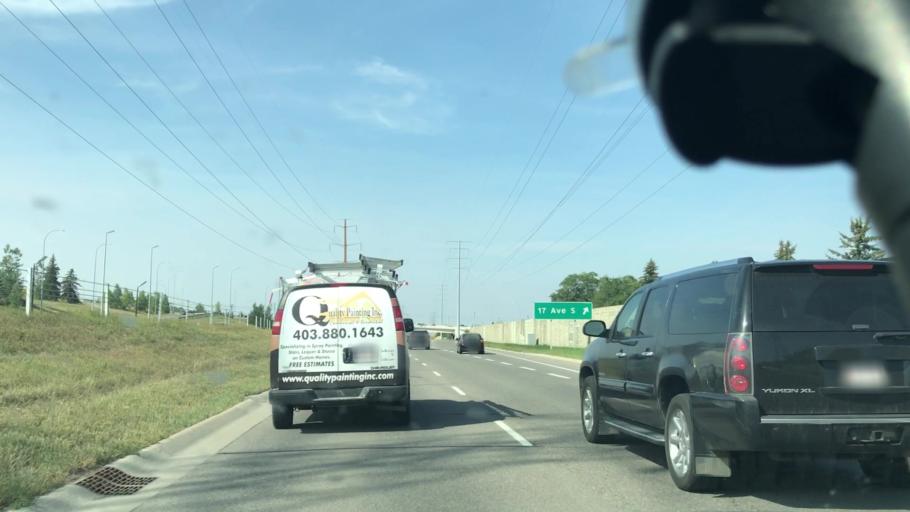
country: CA
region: Alberta
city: Calgary
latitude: 51.0356
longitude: -114.1642
